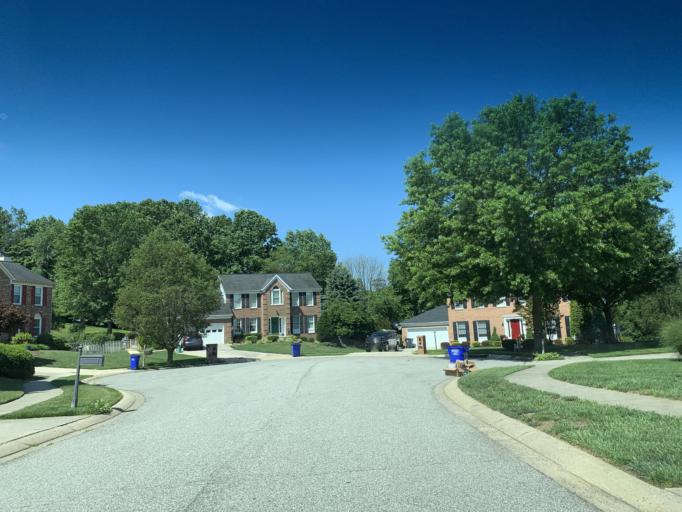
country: US
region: Maryland
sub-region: Harford County
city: South Bel Air
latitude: 39.5265
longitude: -76.3230
